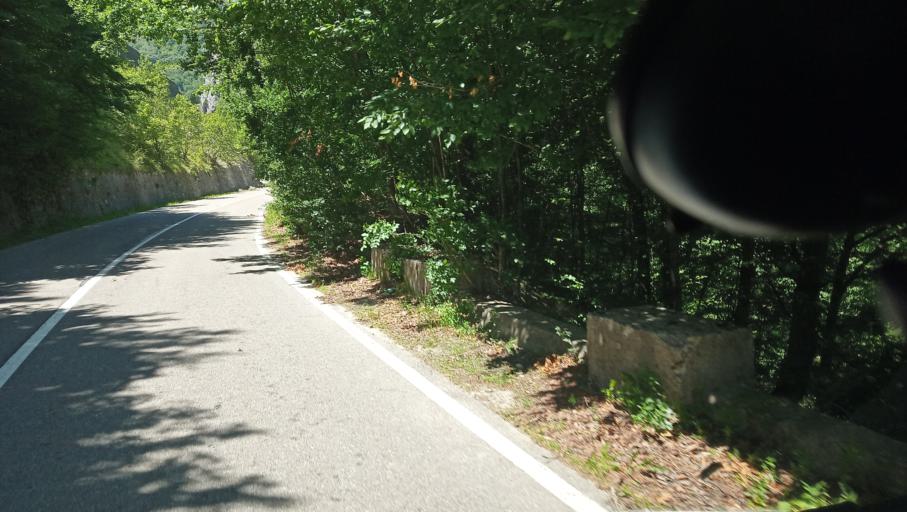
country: RO
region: Mehedinti
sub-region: Comuna Isverna
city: Isverna
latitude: 45.0550
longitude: 22.6032
